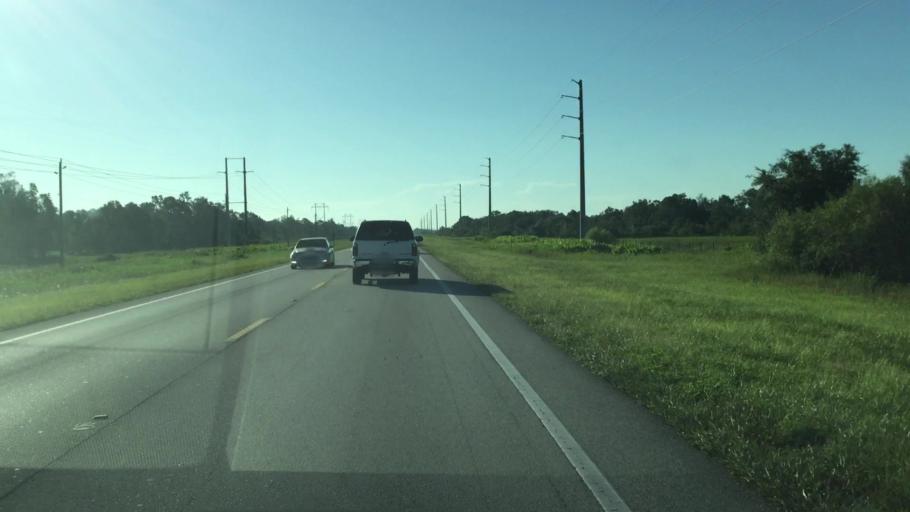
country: US
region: Florida
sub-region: Lee County
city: Gateway
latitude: 26.5730
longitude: -81.6908
